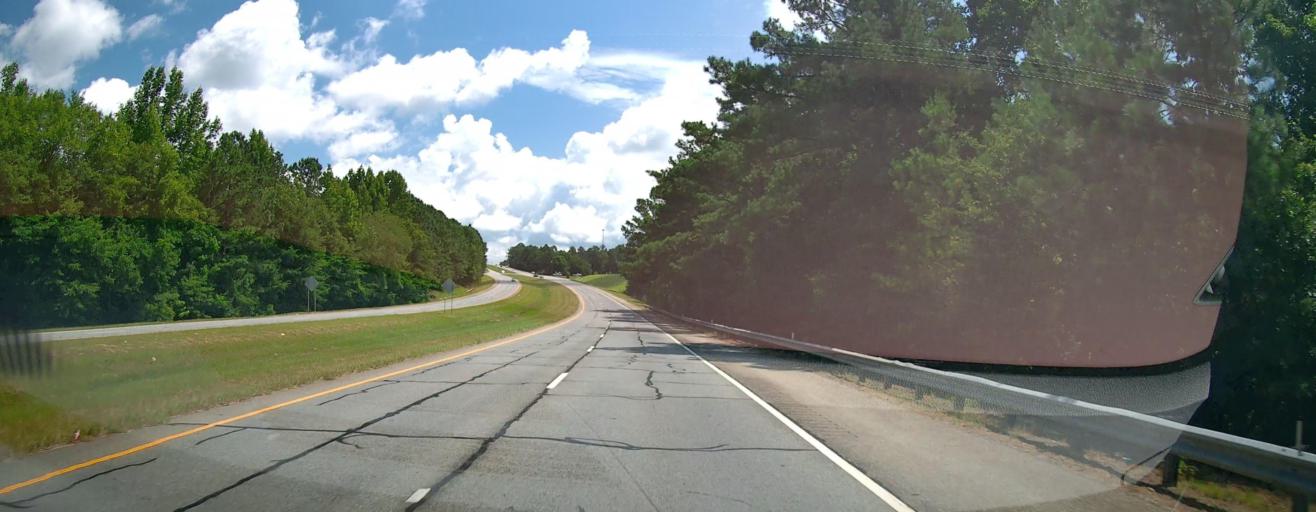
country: US
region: Georgia
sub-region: Bibb County
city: West Point
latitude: 32.8013
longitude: -83.7409
